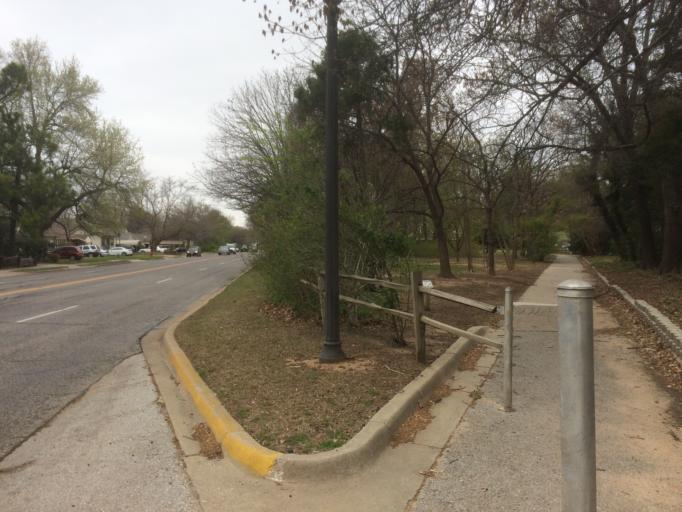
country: US
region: Oklahoma
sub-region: Cleveland County
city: Norman
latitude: 35.2085
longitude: -97.4346
